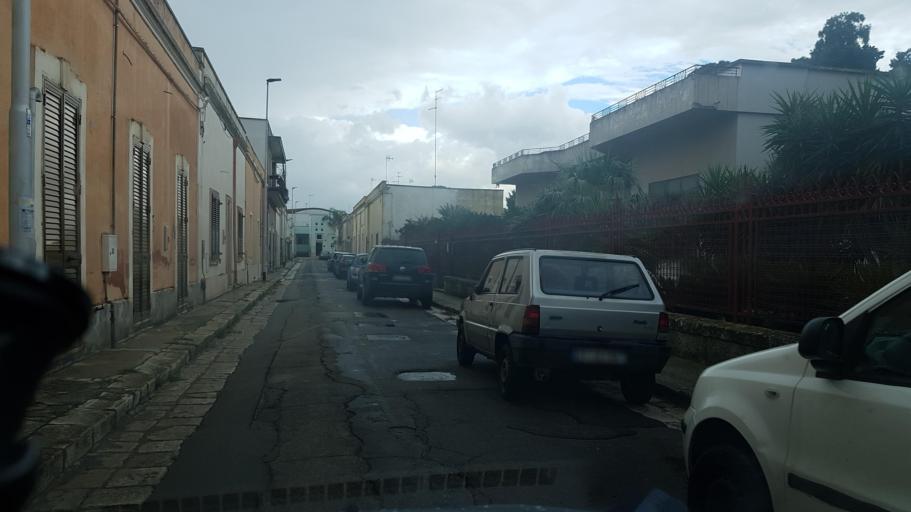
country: IT
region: Apulia
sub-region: Provincia di Lecce
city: Carmiano
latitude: 40.3481
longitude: 18.0460
